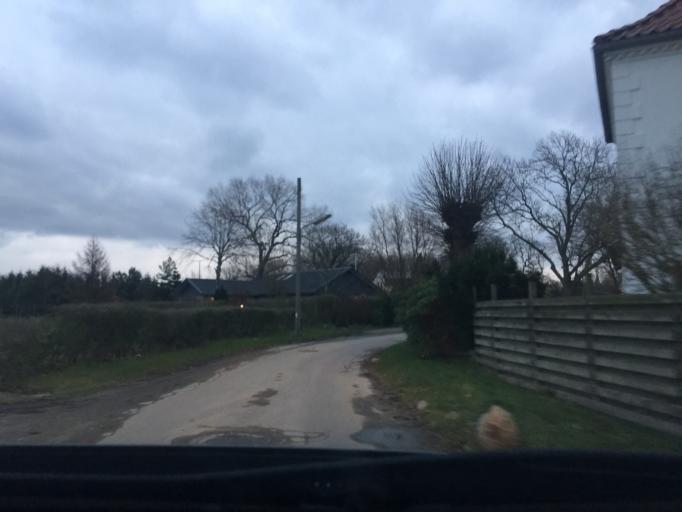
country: DK
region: Capital Region
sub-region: Dragor Kommune
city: Dragor
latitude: 55.5956
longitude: 12.6281
